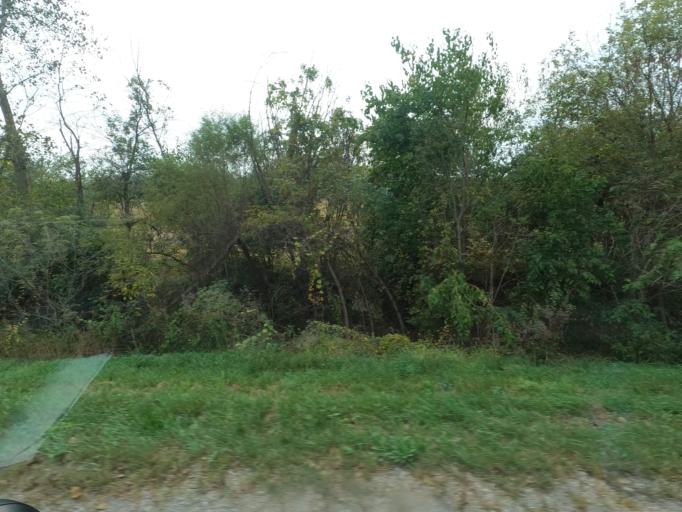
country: US
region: Iowa
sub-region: Jefferson County
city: Fairfield
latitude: 40.8760
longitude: -92.1555
